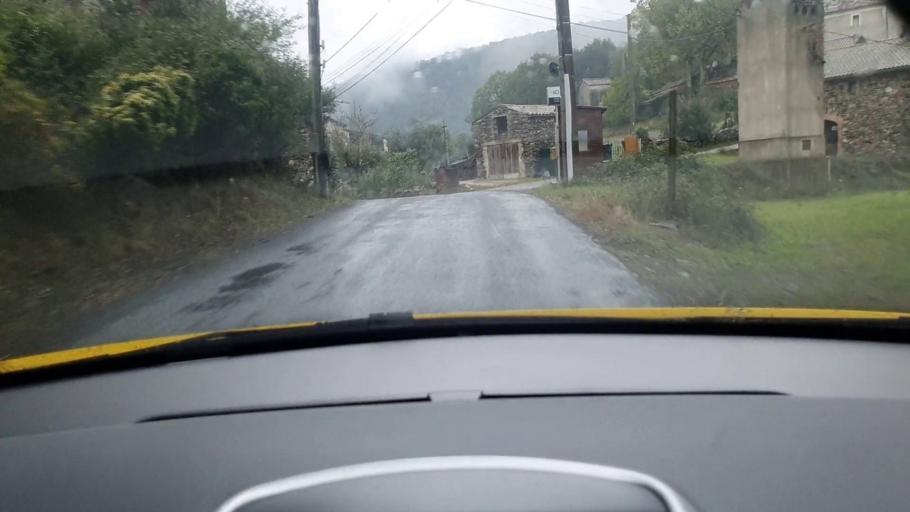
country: FR
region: Languedoc-Roussillon
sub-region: Departement du Gard
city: Sumene
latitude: 44.0083
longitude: 3.7123
